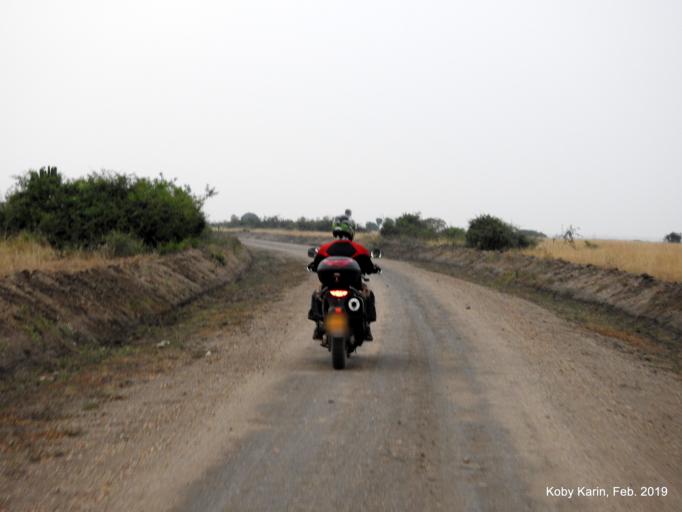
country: UG
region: Western Region
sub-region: Rubirizi District
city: Rubirizi
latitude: -0.0740
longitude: 30.0383
